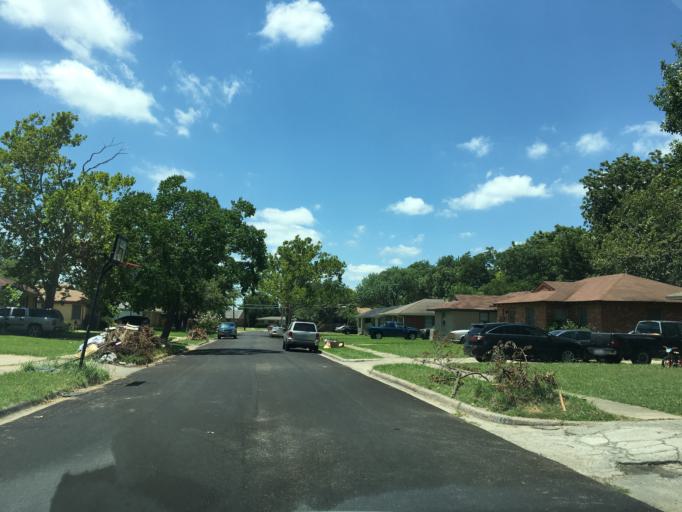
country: US
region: Texas
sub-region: Dallas County
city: Garland
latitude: 32.8370
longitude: -96.6696
